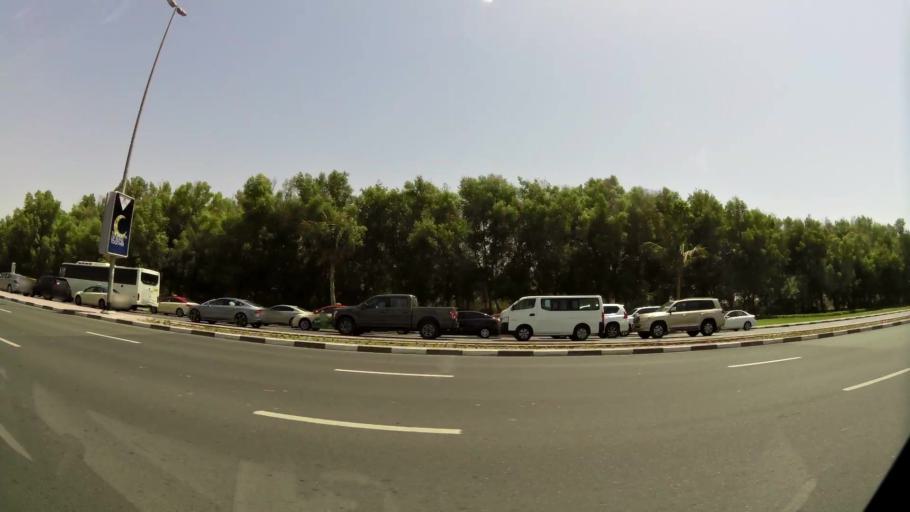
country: AE
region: Dubai
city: Dubai
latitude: 25.1288
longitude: 55.1941
